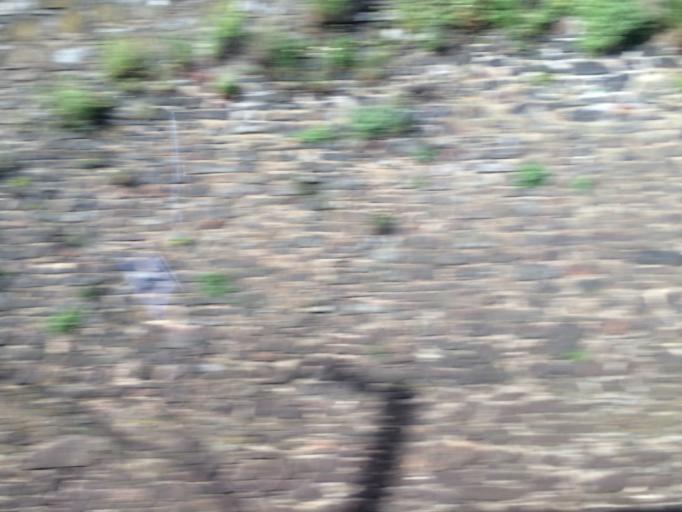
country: DE
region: Rheinland-Pfalz
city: Weiler
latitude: 49.9764
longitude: 7.8755
